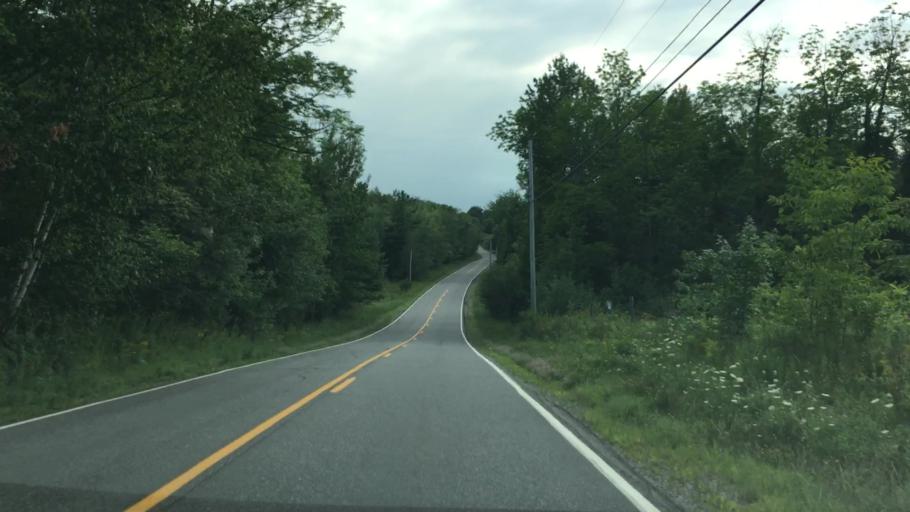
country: US
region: Maine
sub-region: Waldo County
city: Belfast
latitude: 44.3726
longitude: -69.0332
